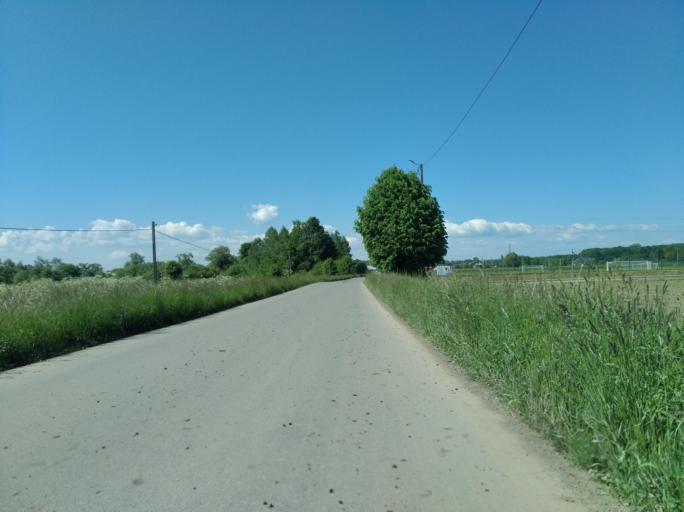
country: PL
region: Subcarpathian Voivodeship
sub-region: Powiat krosnienski
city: Odrzykon
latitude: 49.7366
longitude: 21.7234
